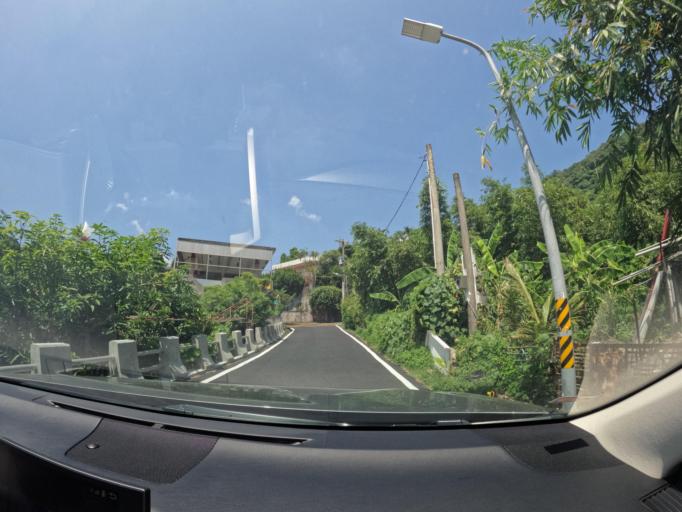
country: TW
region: Taipei
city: Taipei
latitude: 25.1202
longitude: 121.5427
